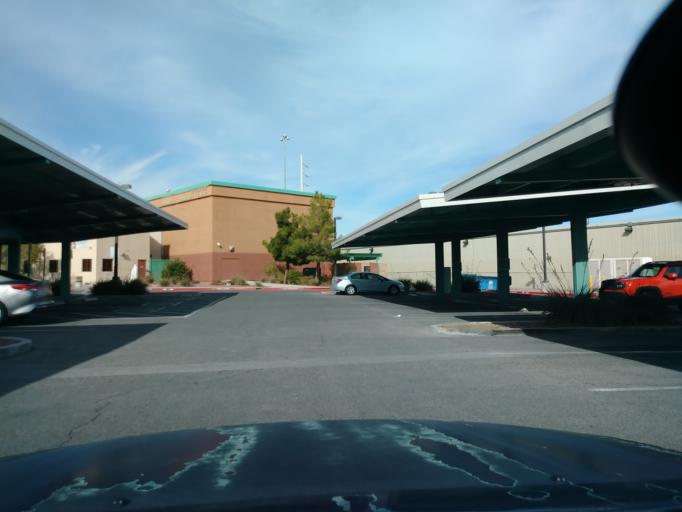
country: US
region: Nevada
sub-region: Clark County
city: Spring Valley
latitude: 36.1727
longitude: -115.2262
